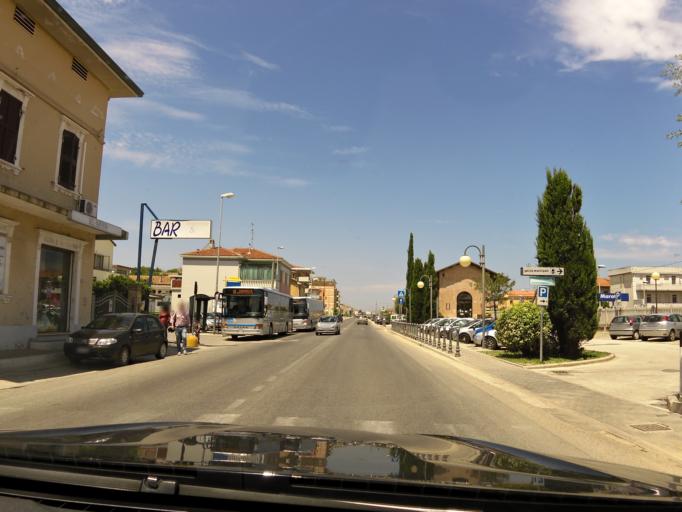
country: IT
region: The Marches
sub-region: Provincia di Pesaro e Urbino
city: Marotta
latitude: 43.7695
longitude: 13.1369
